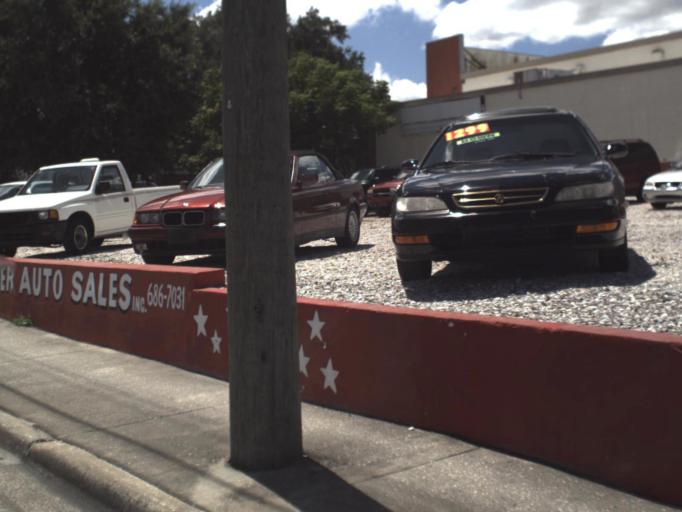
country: US
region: Florida
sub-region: Polk County
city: Lakeland
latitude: 28.0453
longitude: -81.9409
